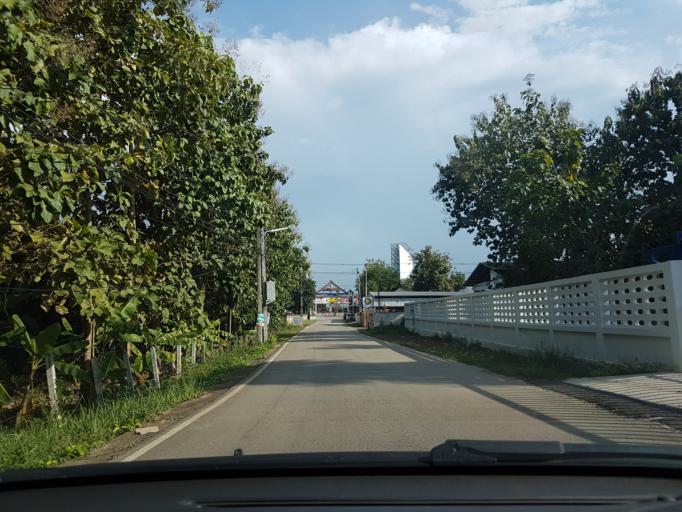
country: TH
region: Lampang
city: Ko Kha
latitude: 18.2167
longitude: 99.4216
